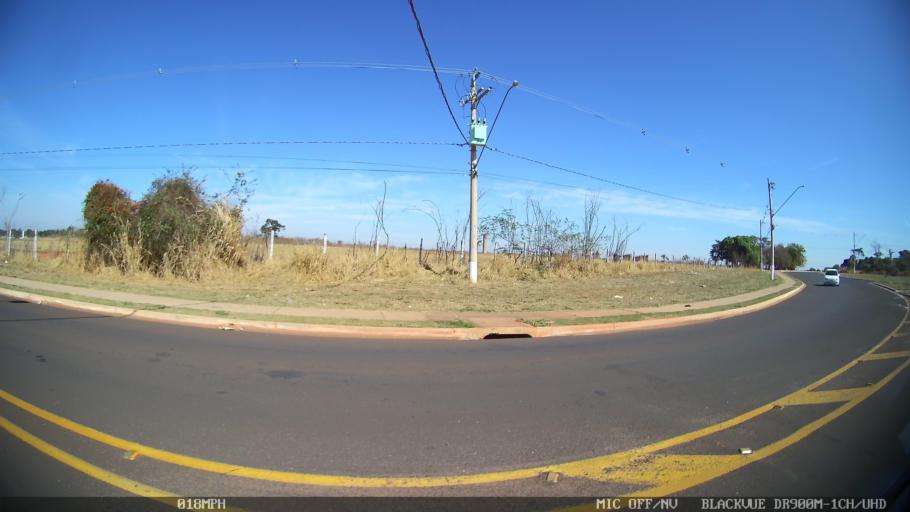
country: BR
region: Sao Paulo
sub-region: Sao Jose Do Rio Preto
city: Sao Jose do Rio Preto
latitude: -20.7513
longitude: -49.4408
